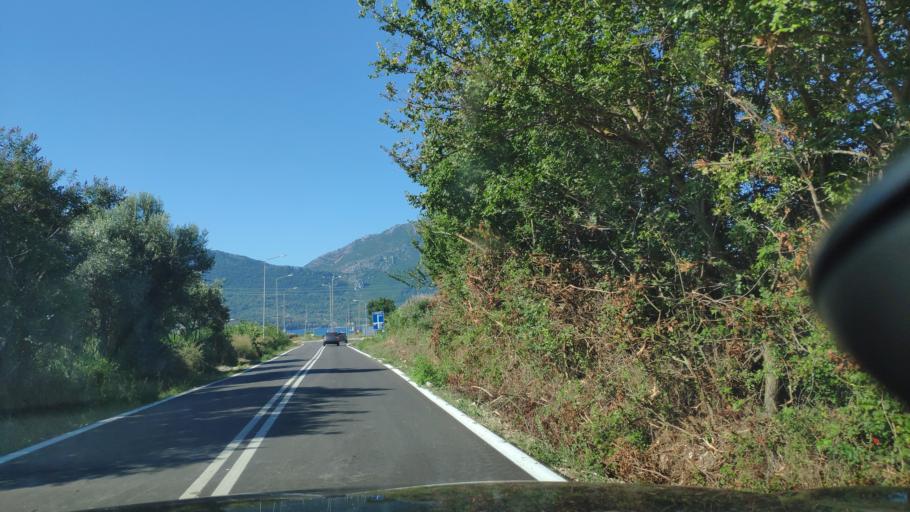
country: GR
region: West Greece
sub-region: Nomos Aitolias kai Akarnanias
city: Kandila
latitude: 38.6777
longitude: 20.9411
